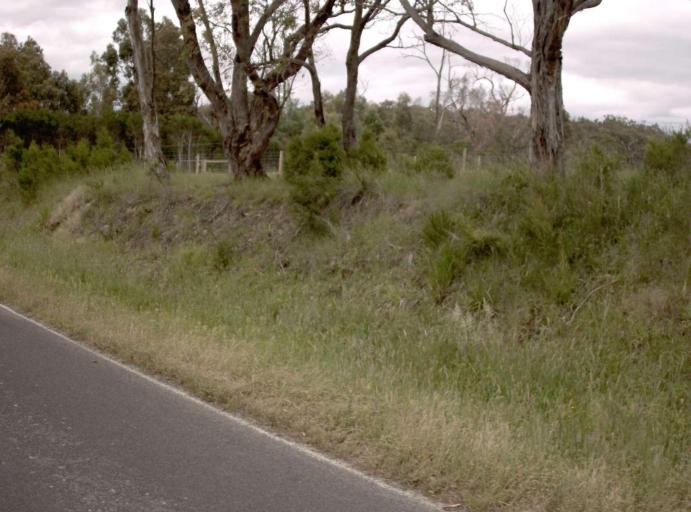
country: AU
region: Victoria
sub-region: Bass Coast
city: North Wonthaggi
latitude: -38.5344
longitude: 145.6989
